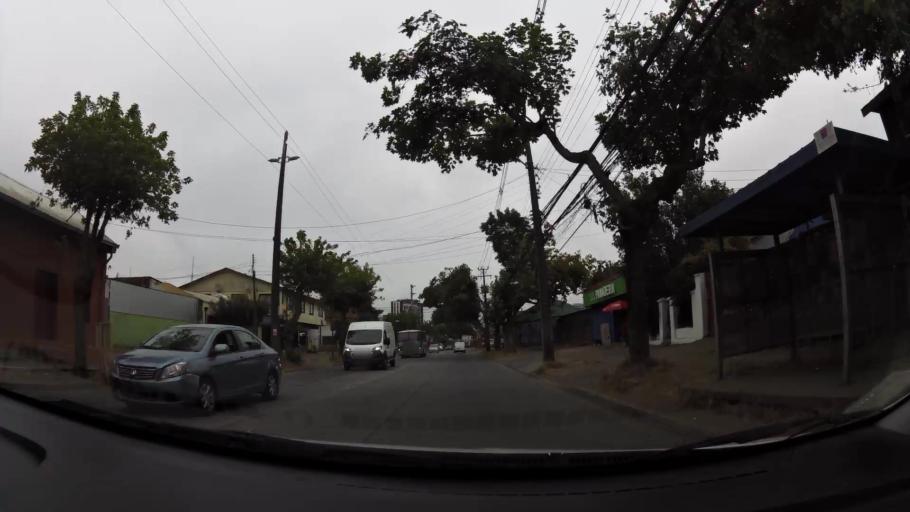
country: CL
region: Biobio
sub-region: Provincia de Concepcion
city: Concepcion
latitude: -36.8128
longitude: -73.0374
